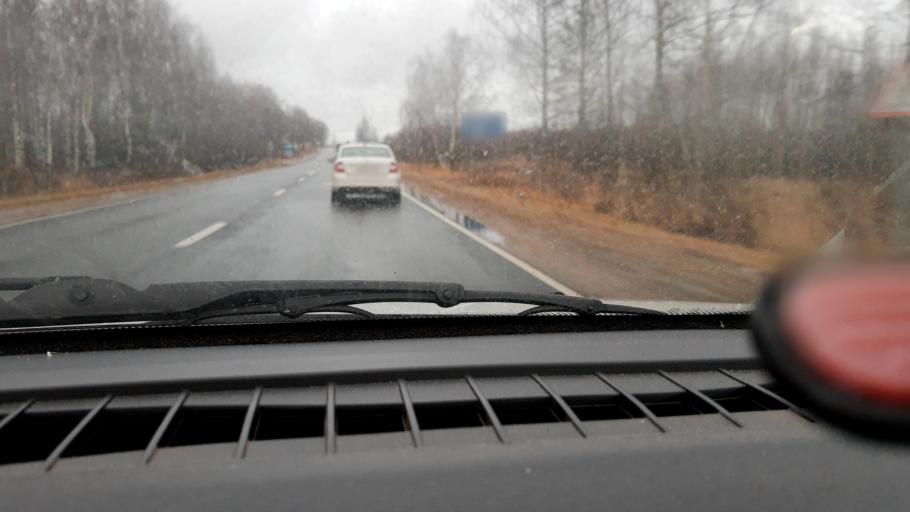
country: RU
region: Nizjnij Novgorod
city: Krasnyye Baki
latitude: 57.0921
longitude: 45.1493
